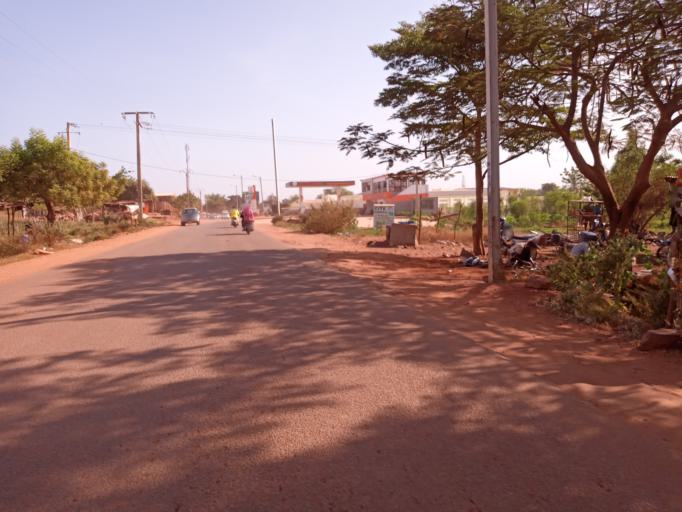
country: ML
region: Bamako
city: Bamako
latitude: 12.6244
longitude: -7.9552
